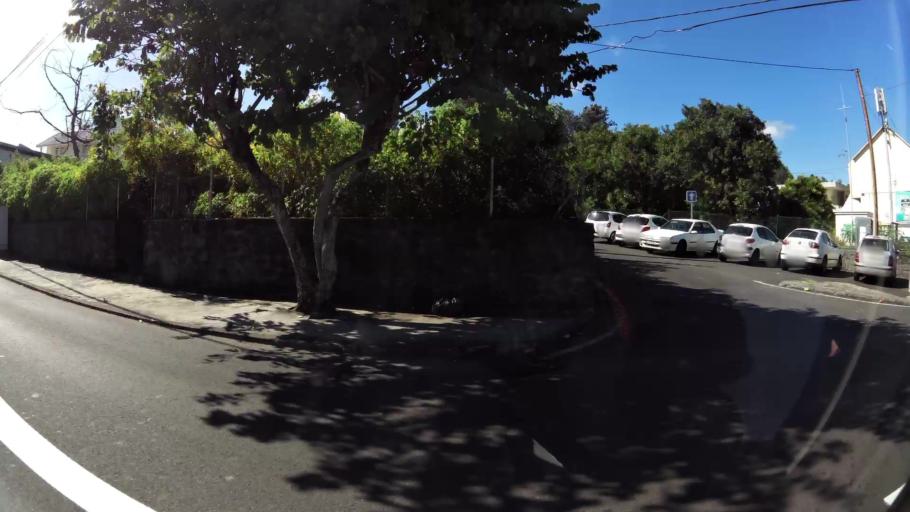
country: RE
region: Reunion
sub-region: Reunion
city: Le Tampon
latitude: -21.2760
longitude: 55.5136
